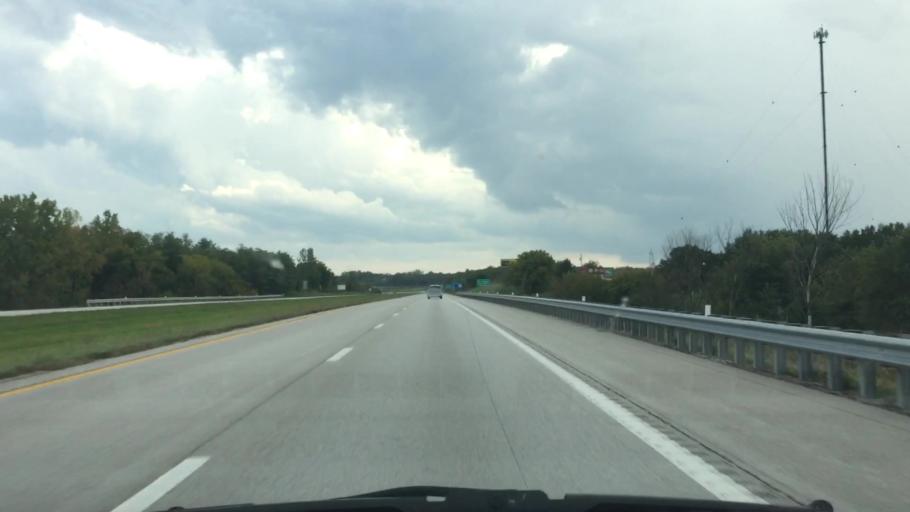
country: US
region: Missouri
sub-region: Clinton County
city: Cameron
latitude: 39.7642
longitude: -94.2167
